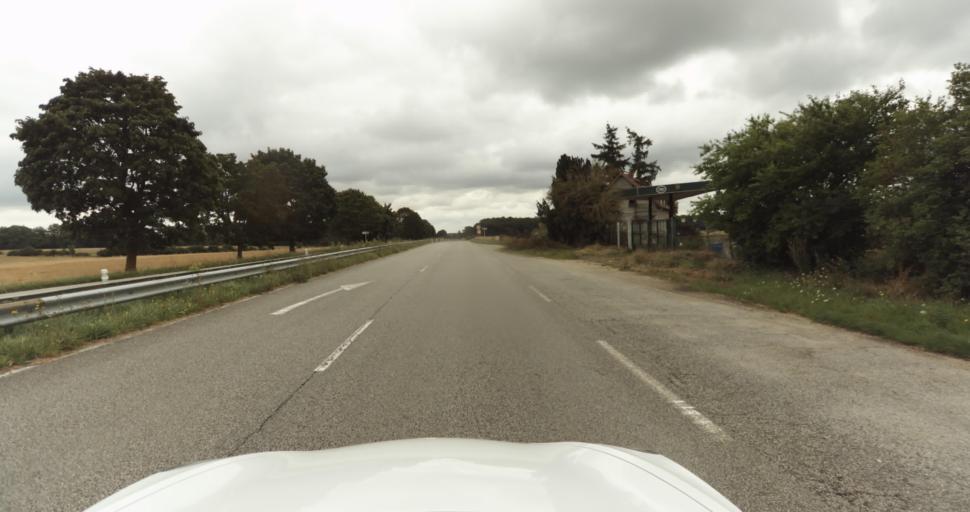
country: FR
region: Haute-Normandie
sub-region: Departement de l'Eure
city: Saint-Sebastien-de-Morsent
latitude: 49.0303
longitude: 1.1019
